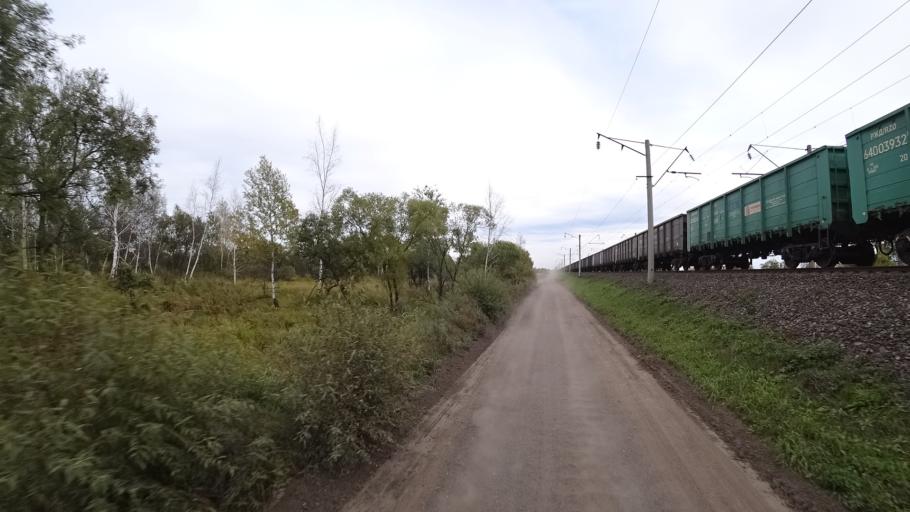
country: RU
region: Amur
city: Arkhara
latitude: 49.3614
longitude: 130.1489
